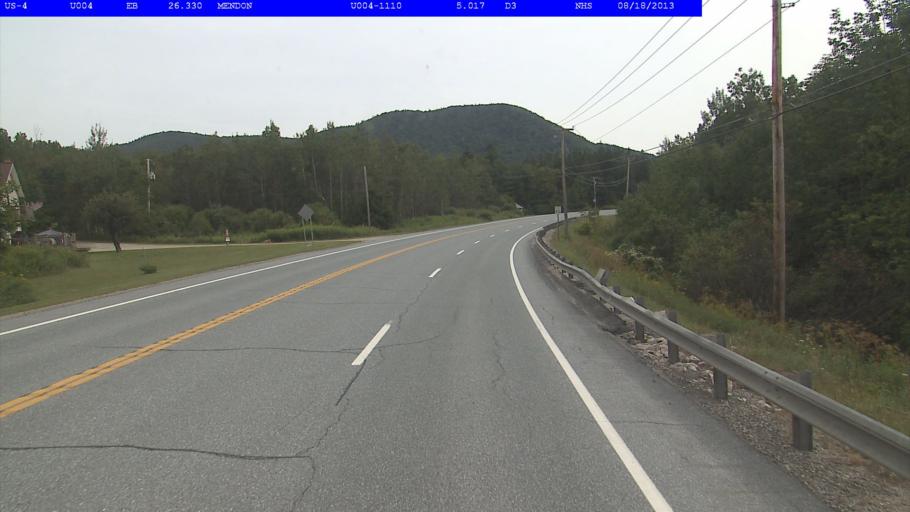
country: US
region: Vermont
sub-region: Rutland County
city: Rutland
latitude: 43.6653
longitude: -72.8631
